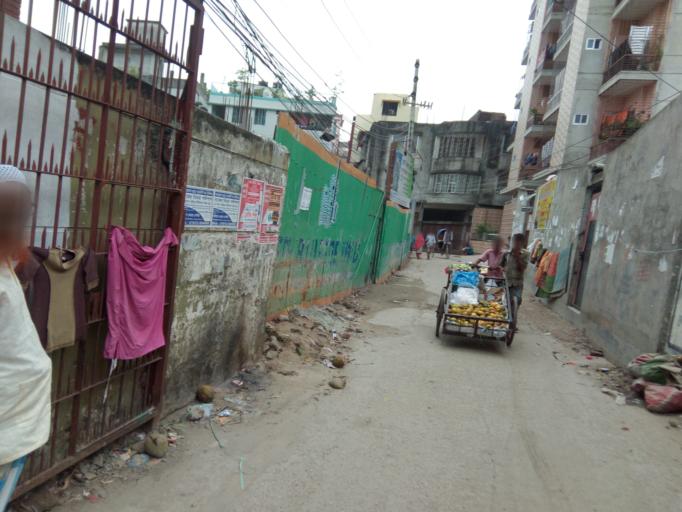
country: BD
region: Dhaka
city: Paltan
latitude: 23.7610
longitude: 90.4156
